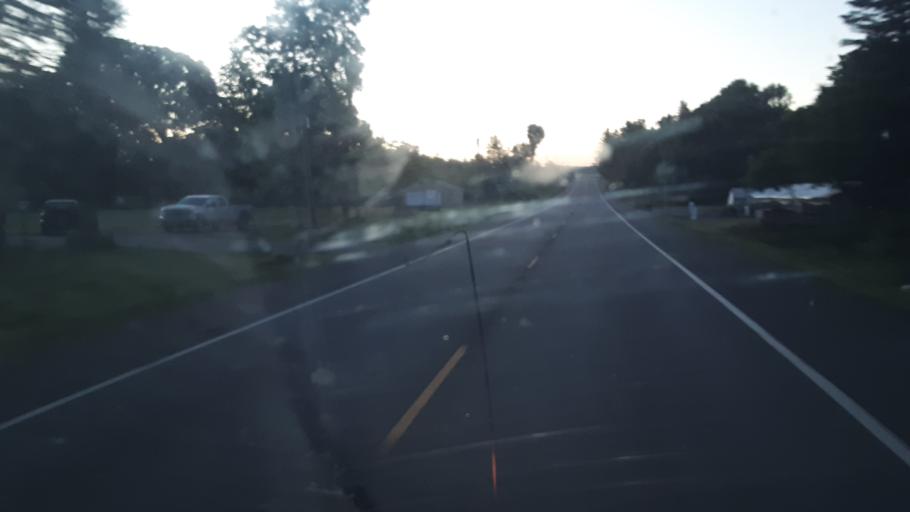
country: US
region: New York
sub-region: Montgomery County
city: Hagaman
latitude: 42.9683
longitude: -74.0998
